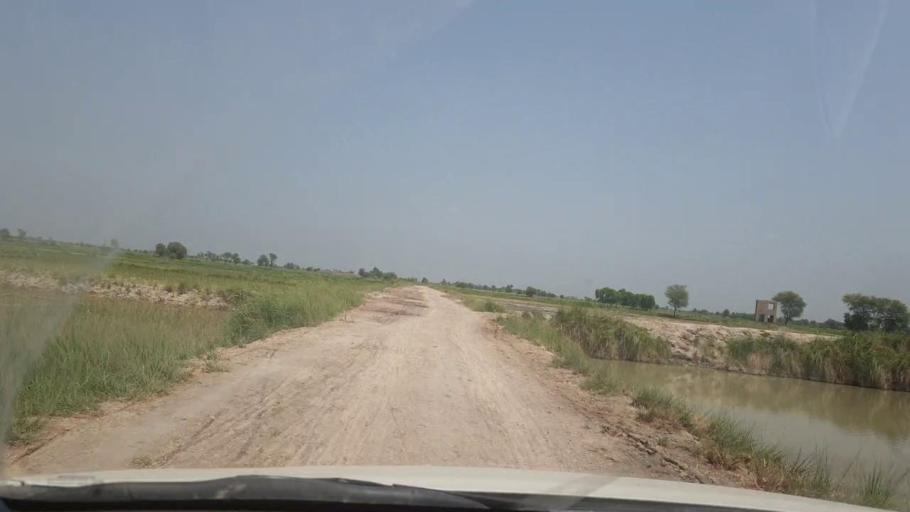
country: PK
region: Sindh
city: Lakhi
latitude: 27.8650
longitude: 68.7198
